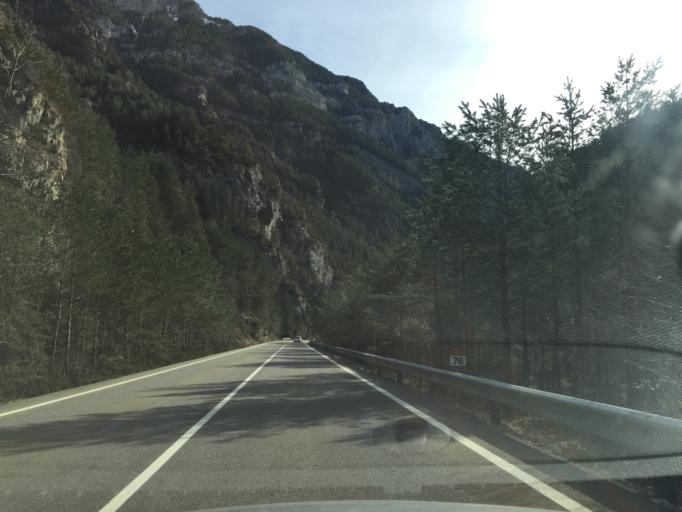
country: ES
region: Aragon
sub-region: Provincia de Huesca
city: Bielsa
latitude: 42.6047
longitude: 0.2395
